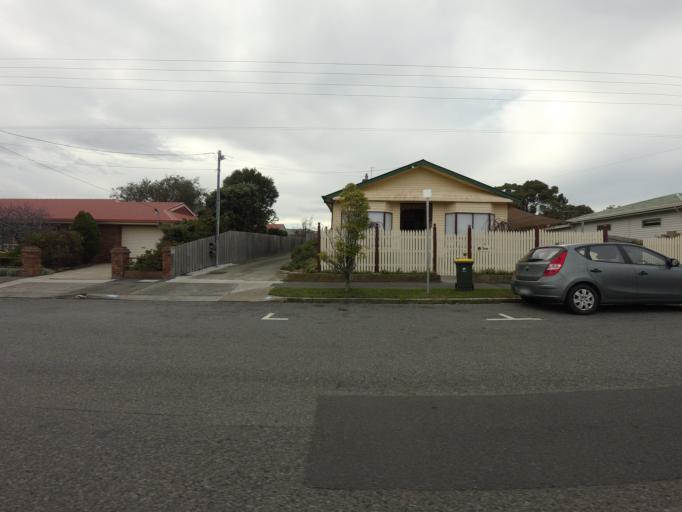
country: AU
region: Tasmania
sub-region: Clarence
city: Bellerive
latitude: -42.8768
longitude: 147.3705
